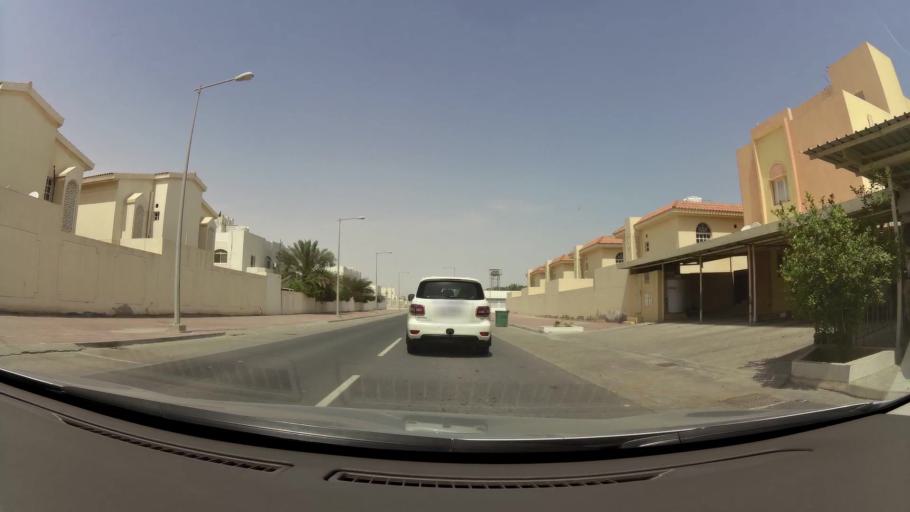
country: QA
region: Baladiyat ad Dawhah
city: Doha
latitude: 25.3262
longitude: 51.4892
